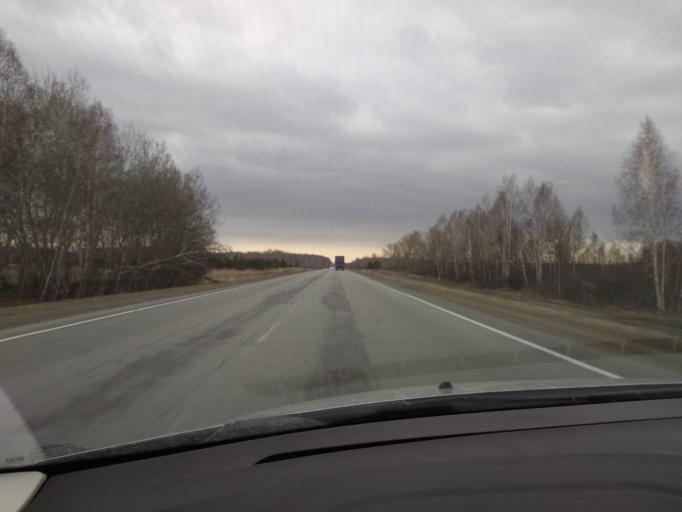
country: RU
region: Chelyabinsk
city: Tyubuk
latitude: 55.8767
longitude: 61.1472
